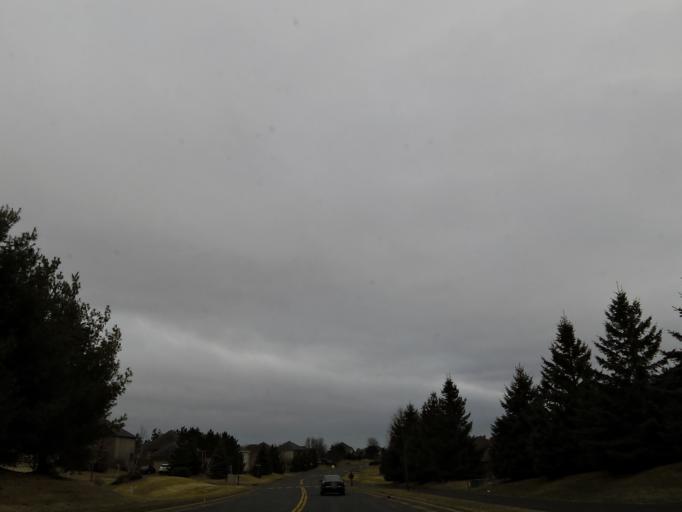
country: US
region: Wisconsin
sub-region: Saint Croix County
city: Hudson
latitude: 44.9758
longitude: -92.7309
